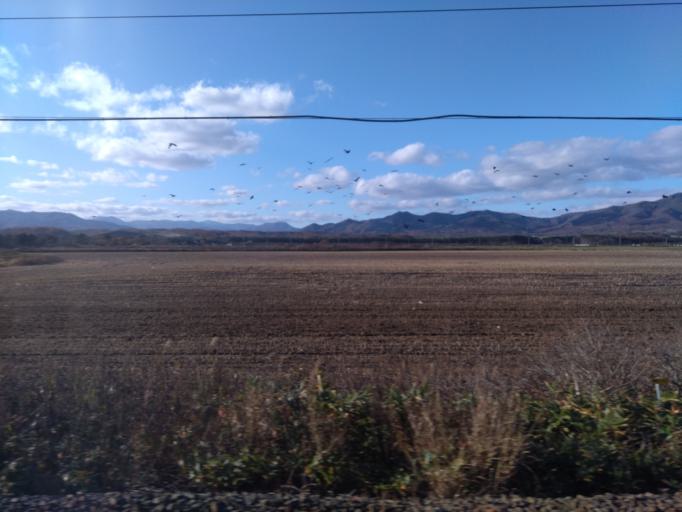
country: JP
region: Hokkaido
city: Niseko Town
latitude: 42.5406
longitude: 140.4063
